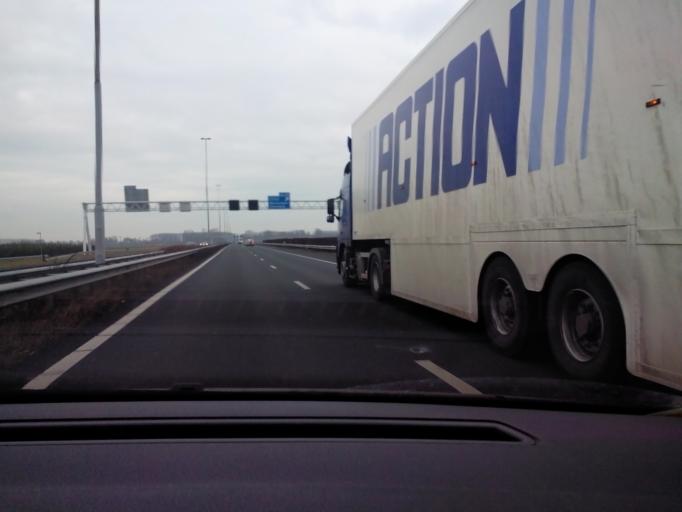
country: NL
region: North Brabant
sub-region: Gemeente Woudrichem
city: Almkerk
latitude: 51.7873
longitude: 4.9289
